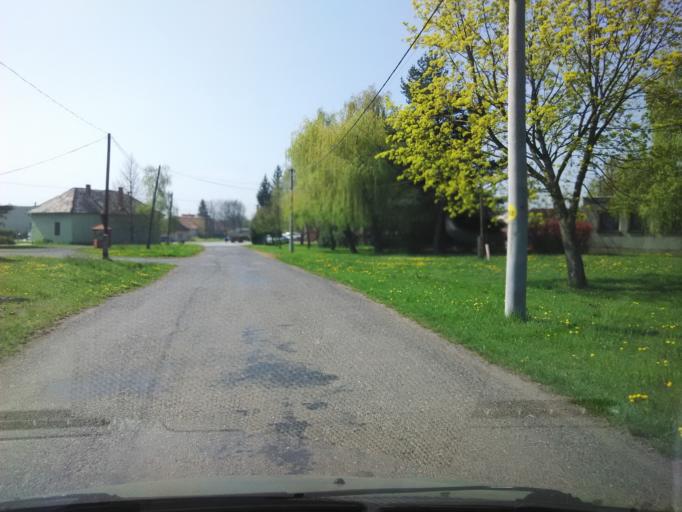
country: SK
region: Nitriansky
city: Levice
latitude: 48.2801
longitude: 18.6416
